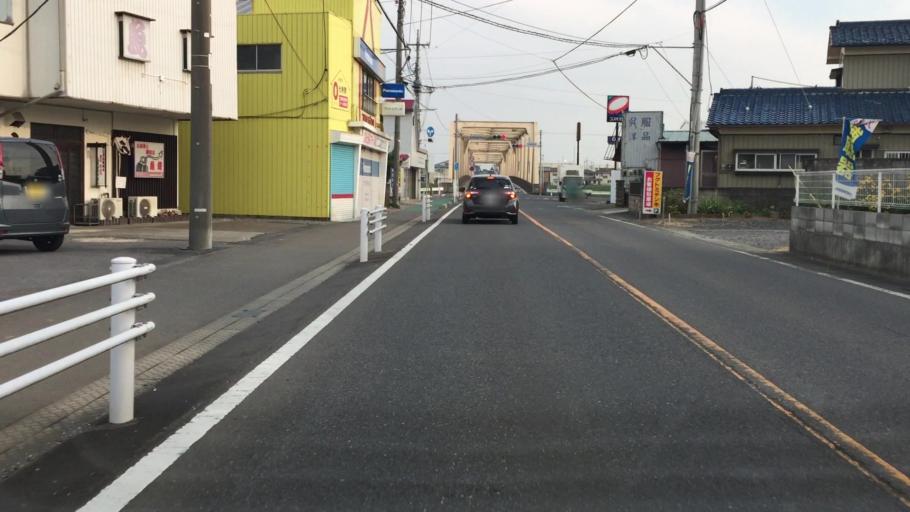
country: JP
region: Tochigi
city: Fujioka
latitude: 36.2667
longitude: 139.6502
